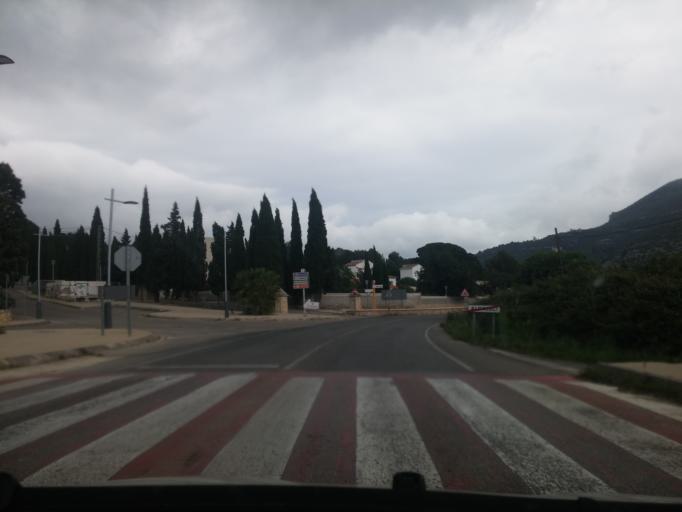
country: ES
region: Valencia
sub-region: Provincia de Alicante
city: Alcalali
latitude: 38.7524
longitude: -0.0415
